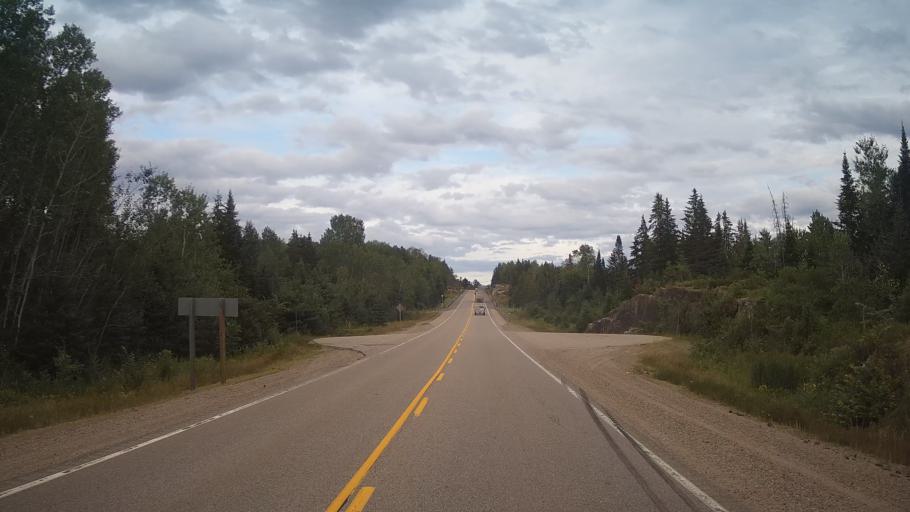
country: CA
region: Ontario
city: Deep River
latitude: 46.2222
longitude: -78.0638
